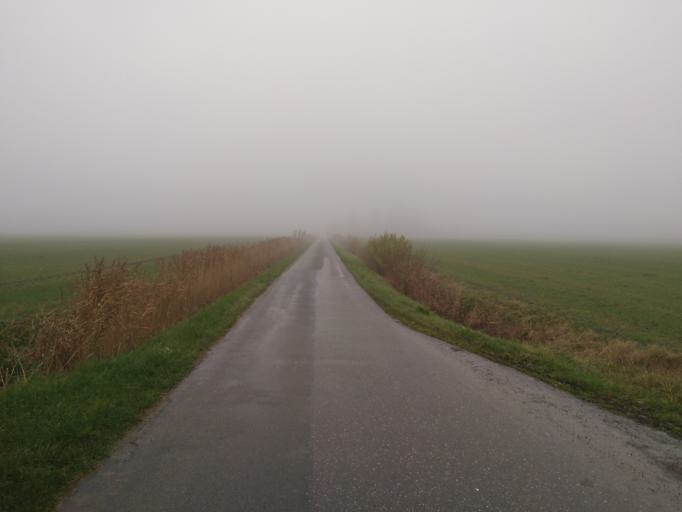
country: DE
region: Schleswig-Holstein
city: Uelvesbull
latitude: 54.4148
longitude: 8.9505
